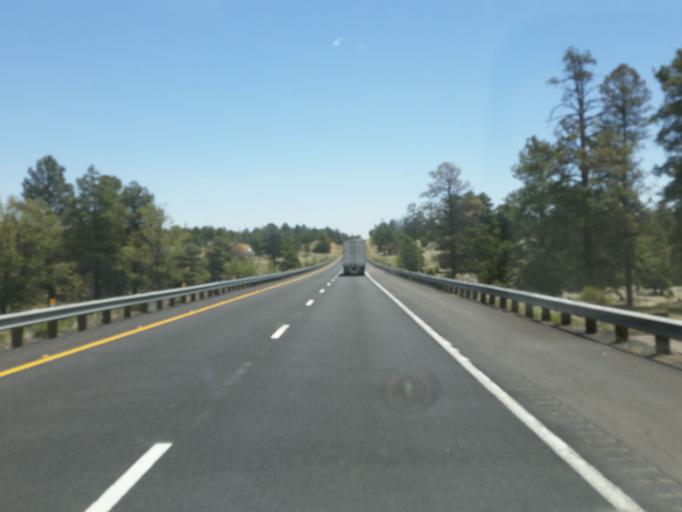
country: US
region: Arizona
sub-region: Coconino County
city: Flagstaff
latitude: 35.2148
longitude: -111.5452
